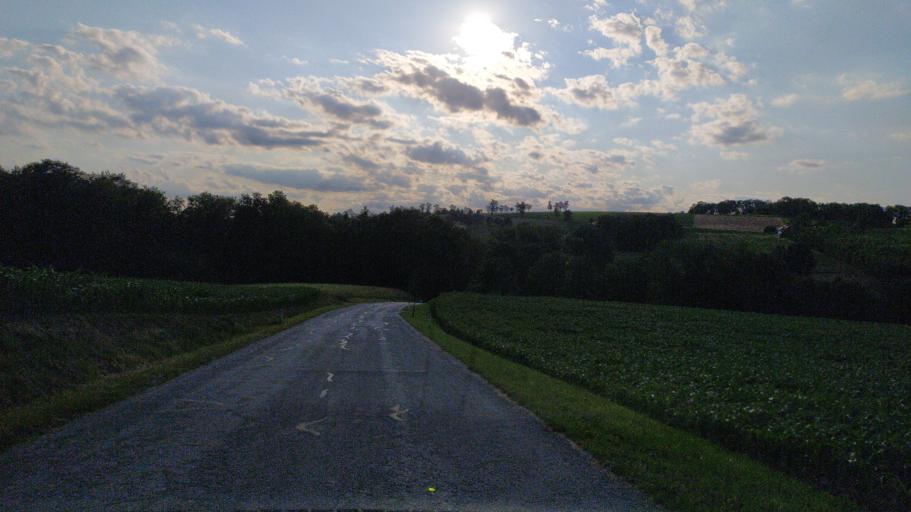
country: AT
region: Lower Austria
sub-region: Politischer Bezirk Amstetten
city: Strengberg
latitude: 48.1492
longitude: 14.6845
